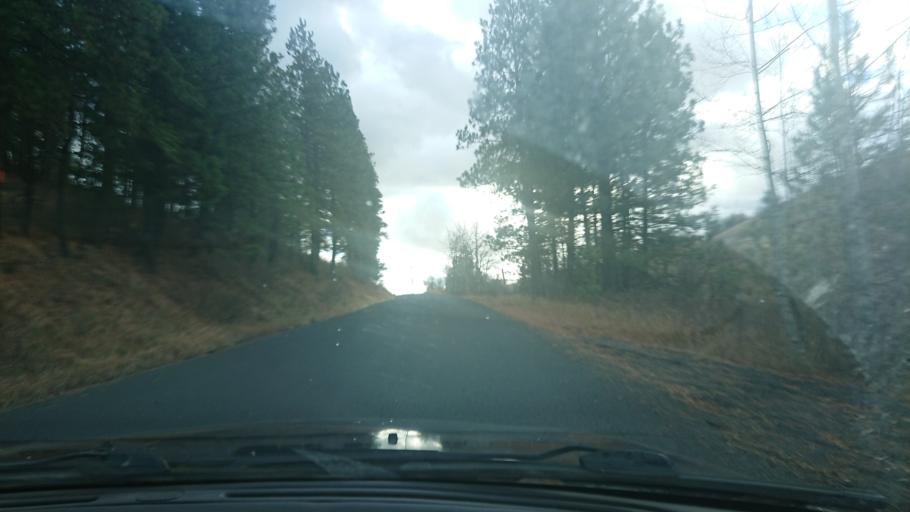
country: US
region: Idaho
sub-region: Latah County
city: Moscow
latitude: 46.6985
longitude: -116.8632
